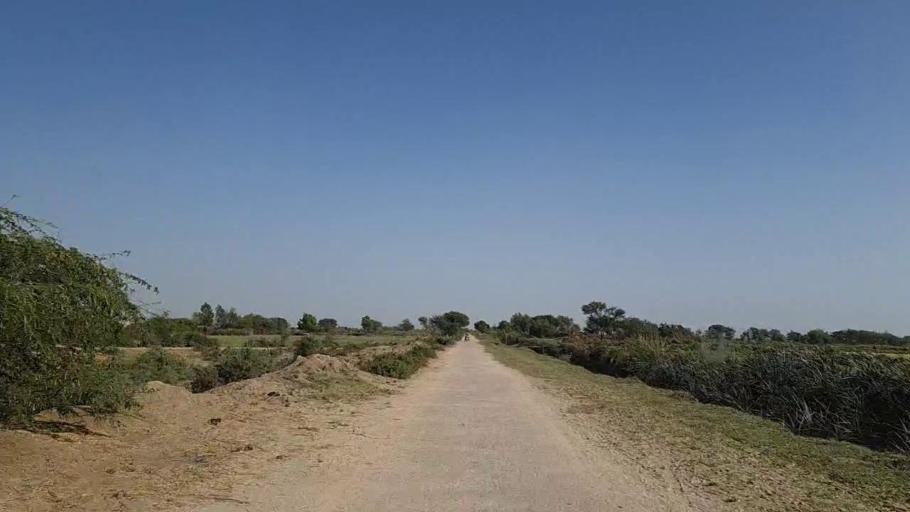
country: PK
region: Sindh
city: Chuhar Jamali
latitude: 24.4855
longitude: 68.0956
